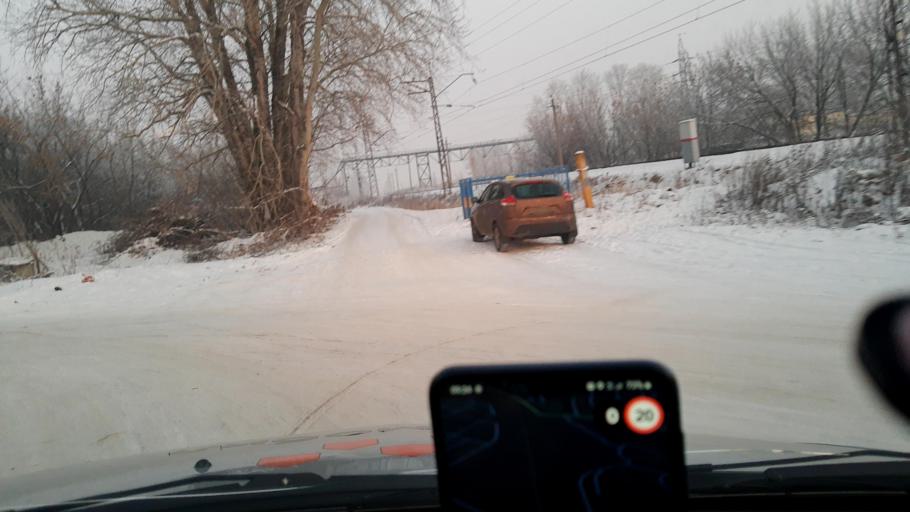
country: RU
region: Bashkortostan
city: Ufa
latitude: 54.8289
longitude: 56.1047
